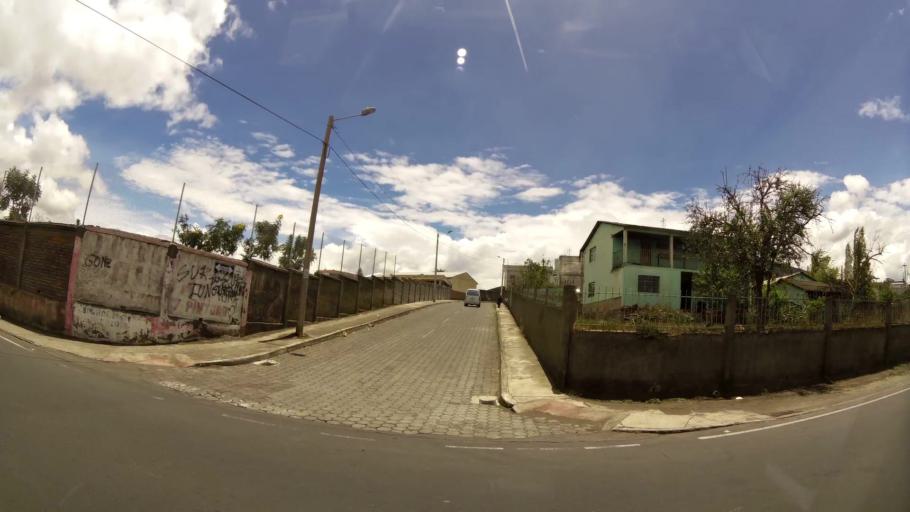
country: EC
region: Tungurahua
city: Pelileo
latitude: -1.3256
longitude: -78.5455
